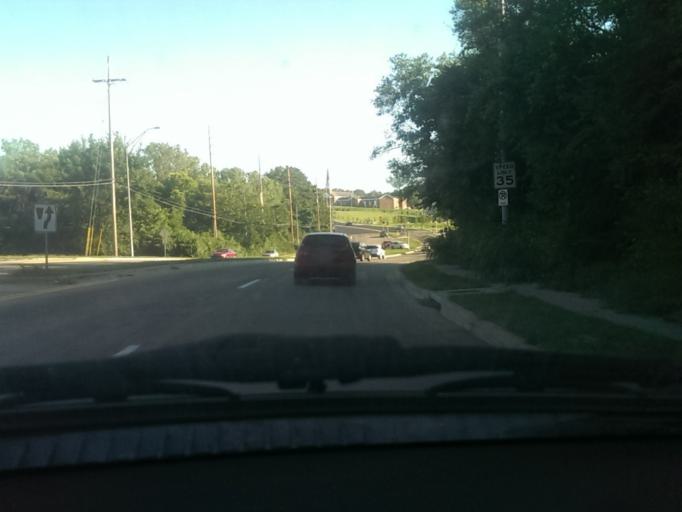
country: US
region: Kansas
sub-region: Johnson County
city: Leawood
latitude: 38.9605
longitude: -94.5948
